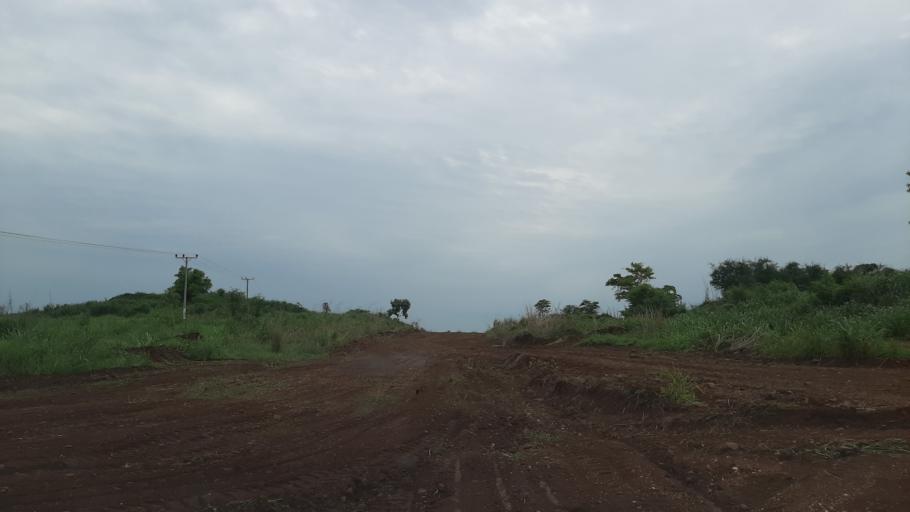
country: ET
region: Gambela
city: Gambela
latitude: 8.2215
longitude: 34.5310
